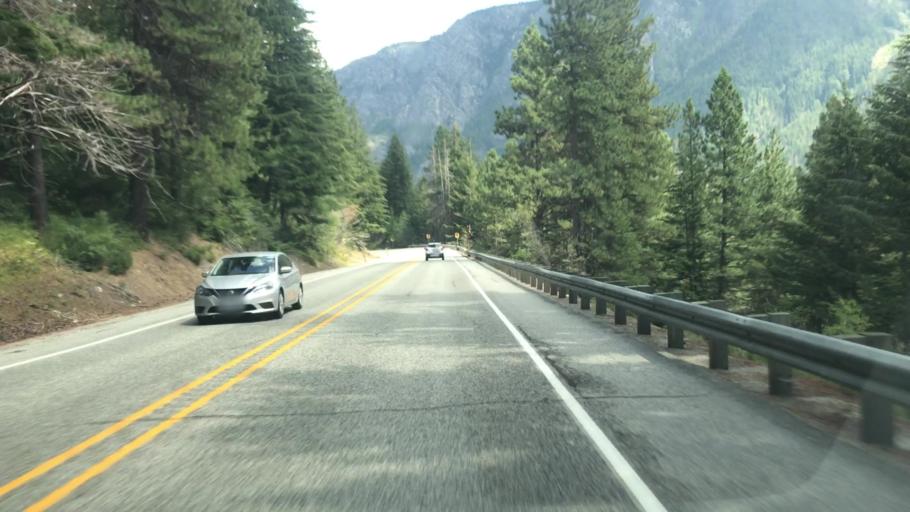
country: US
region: Washington
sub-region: Chelan County
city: Leavenworth
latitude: 47.7801
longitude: -120.9153
